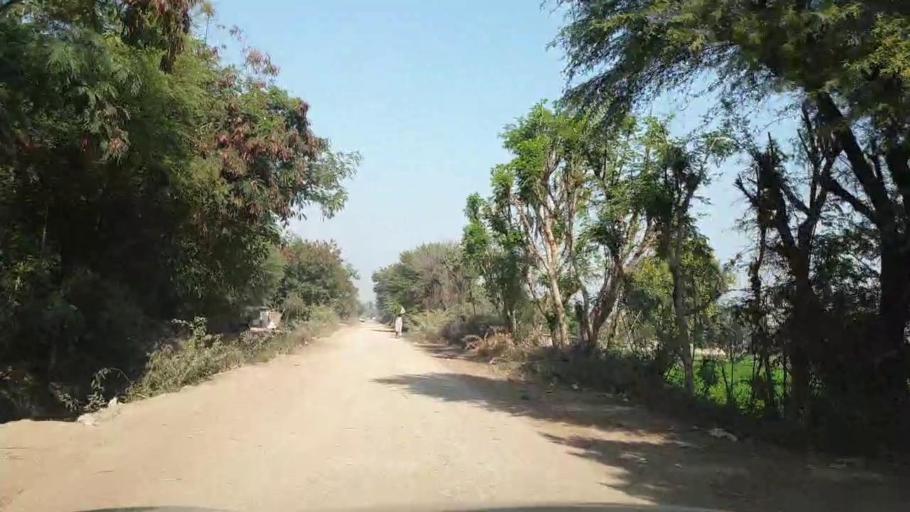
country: PK
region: Sindh
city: Tando Allahyar
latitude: 25.4662
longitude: 68.6931
